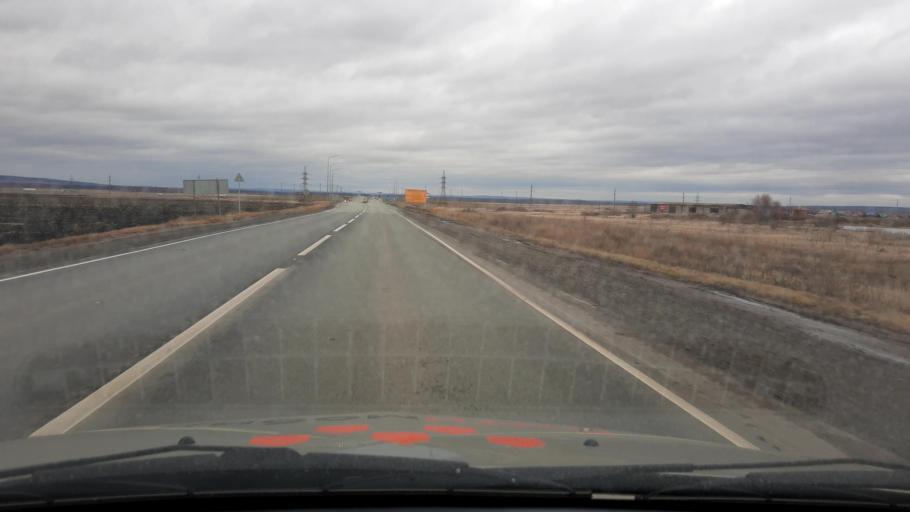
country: RU
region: Bashkortostan
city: Mikhaylovka
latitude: 54.8702
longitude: 55.7077
